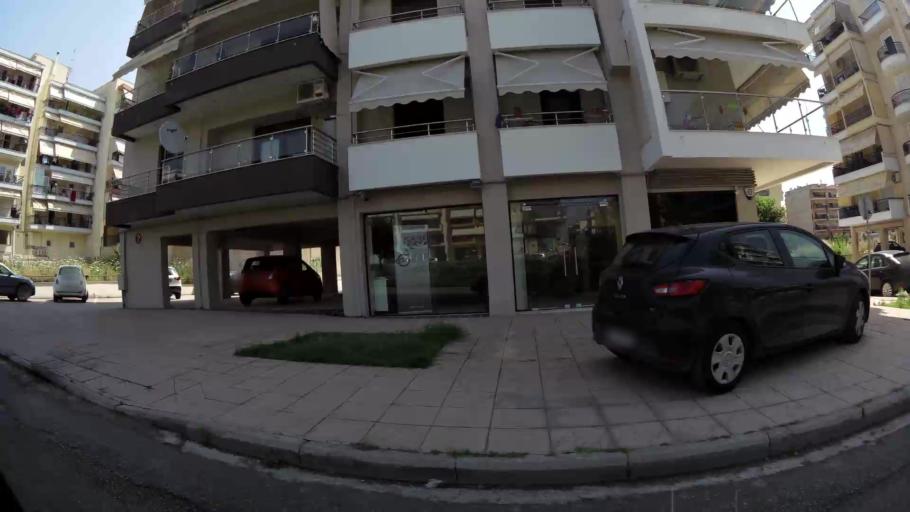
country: GR
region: Central Macedonia
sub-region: Nomos Thessalonikis
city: Evosmos
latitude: 40.6757
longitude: 22.9157
